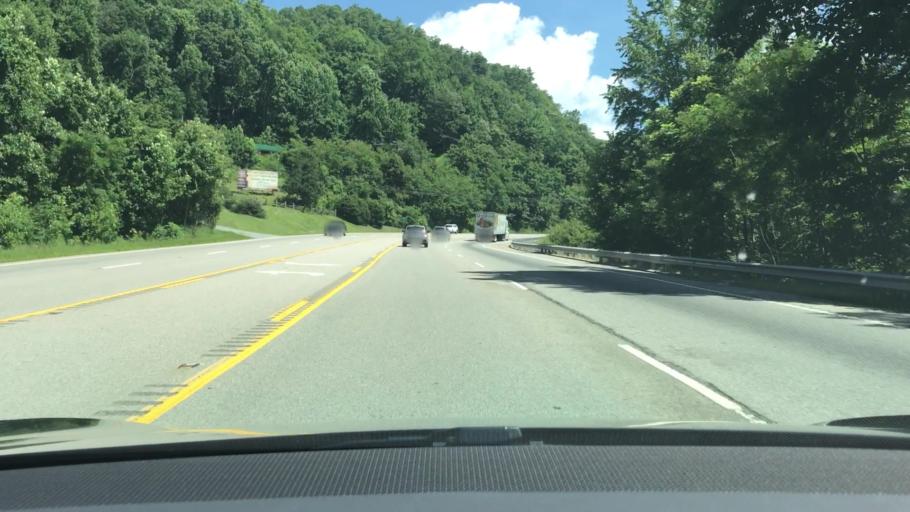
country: US
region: North Carolina
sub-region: Macon County
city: Franklin
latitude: 35.2452
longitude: -83.3208
